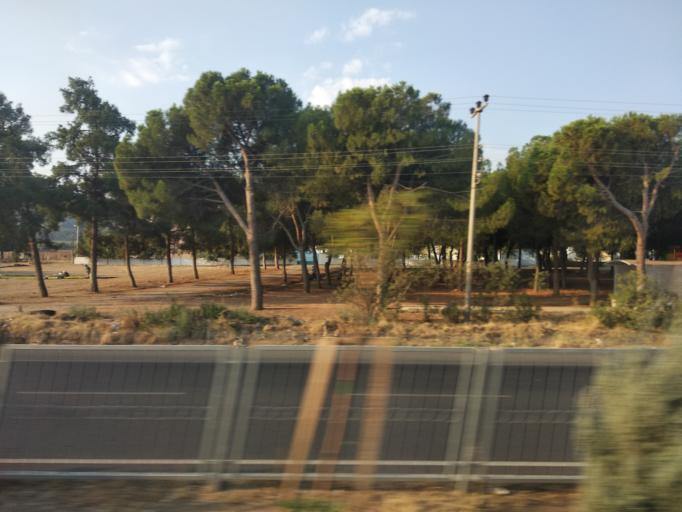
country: TR
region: Manisa
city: Ahmetli
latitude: 38.5054
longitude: 28.0022
